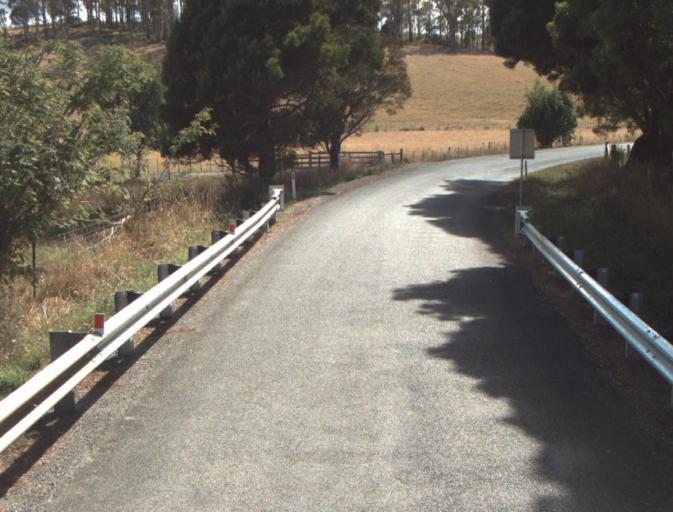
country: AU
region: Tasmania
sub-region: Launceston
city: Mayfield
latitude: -41.2603
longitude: 147.1612
